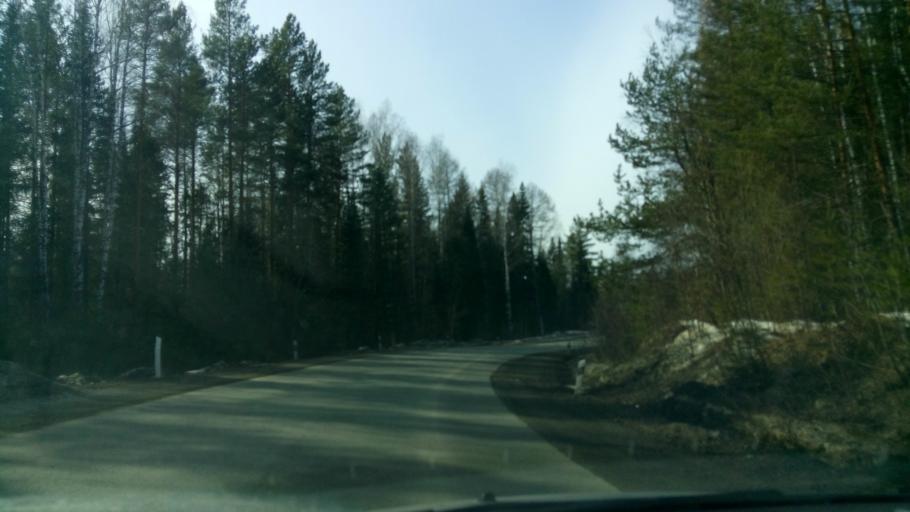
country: RU
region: Sverdlovsk
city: Chernoistochinsk
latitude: 57.7004
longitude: 59.7687
